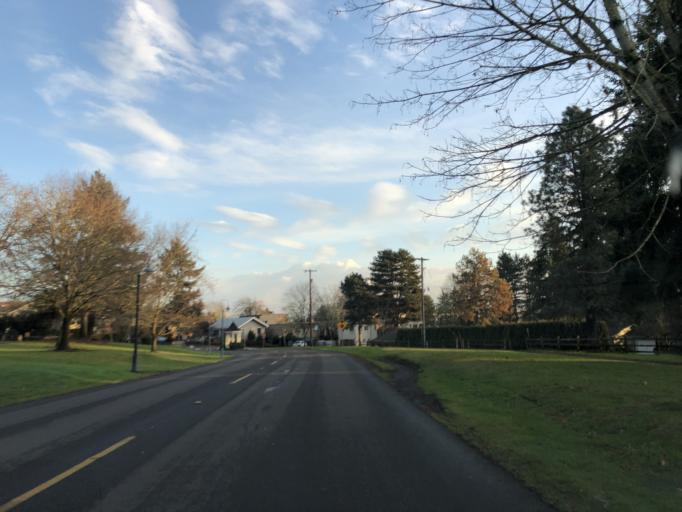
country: US
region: Washington
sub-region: Clark County
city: Vancouver
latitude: 45.6266
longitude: -122.6553
